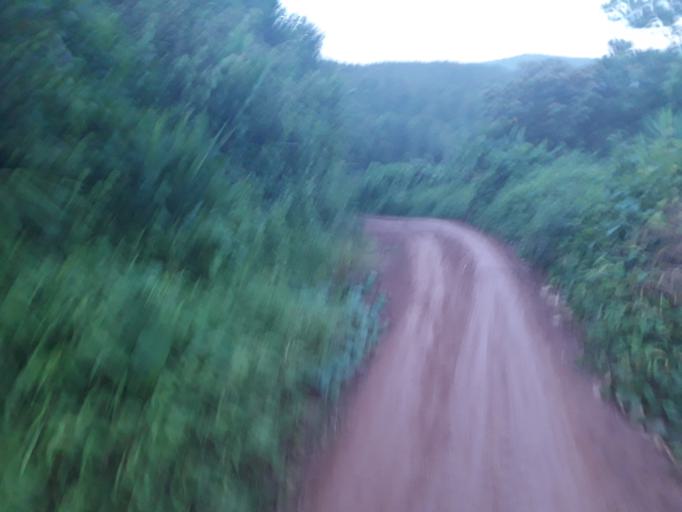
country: CN
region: Yunnan
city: Menglie
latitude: 22.1209
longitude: 101.7736
